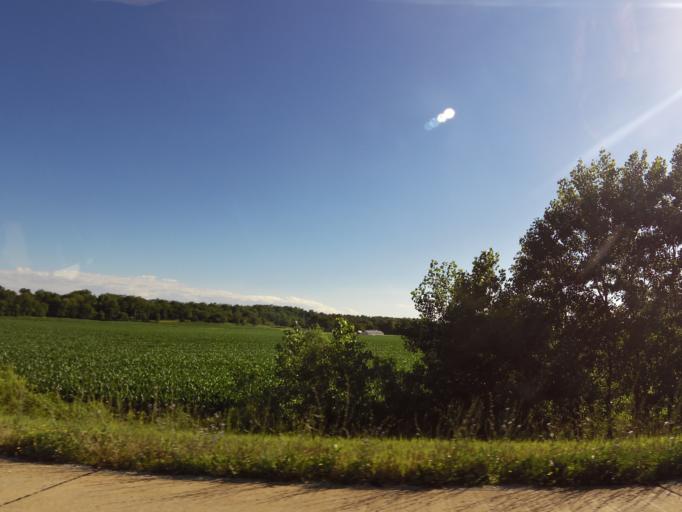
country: US
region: Missouri
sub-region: Ralls County
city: New London
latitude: 39.5187
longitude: -91.3414
